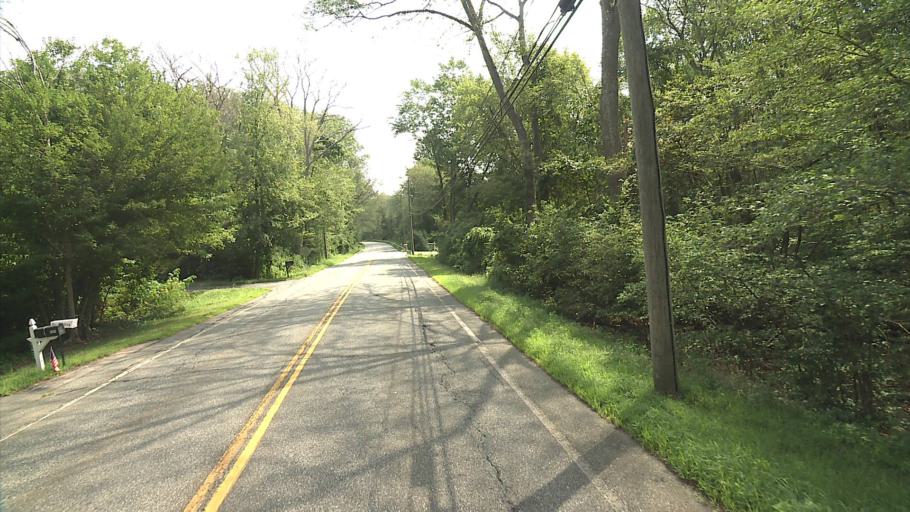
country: US
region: Connecticut
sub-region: New London County
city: Montville Center
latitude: 41.5030
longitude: -72.1977
